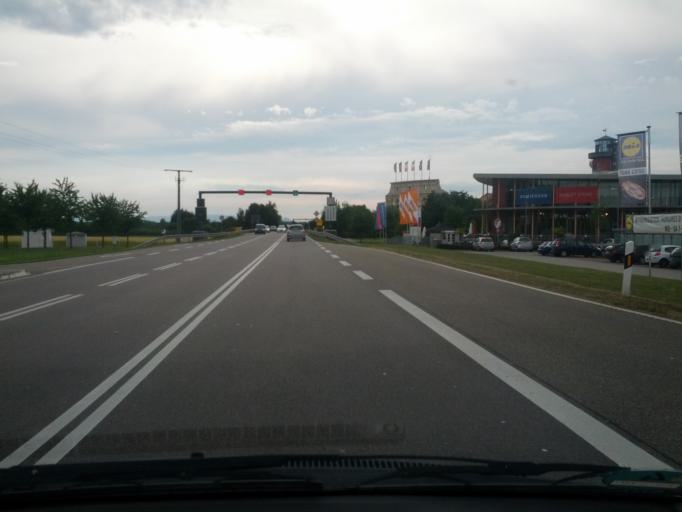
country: DE
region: Baden-Wuerttemberg
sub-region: Freiburg Region
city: Rust
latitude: 48.2587
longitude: 7.7285
